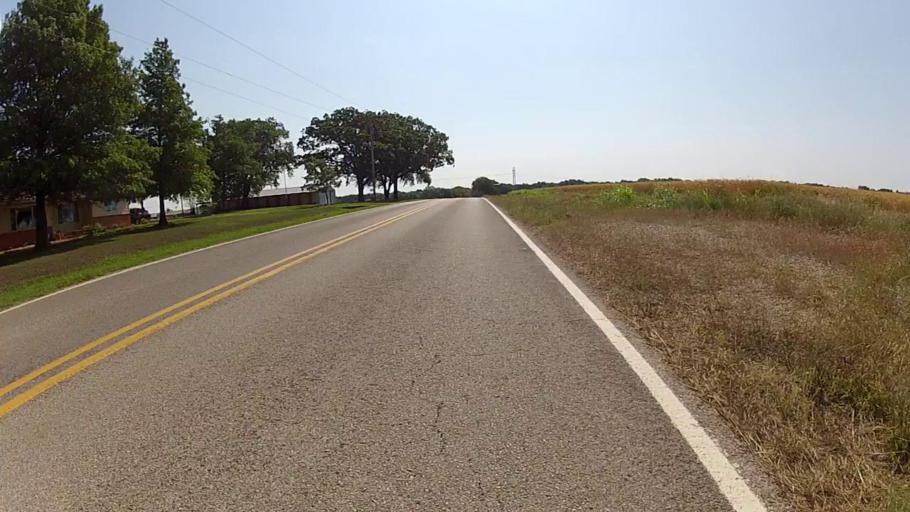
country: US
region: Kansas
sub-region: Montgomery County
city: Independence
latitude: 37.1930
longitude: -95.7409
